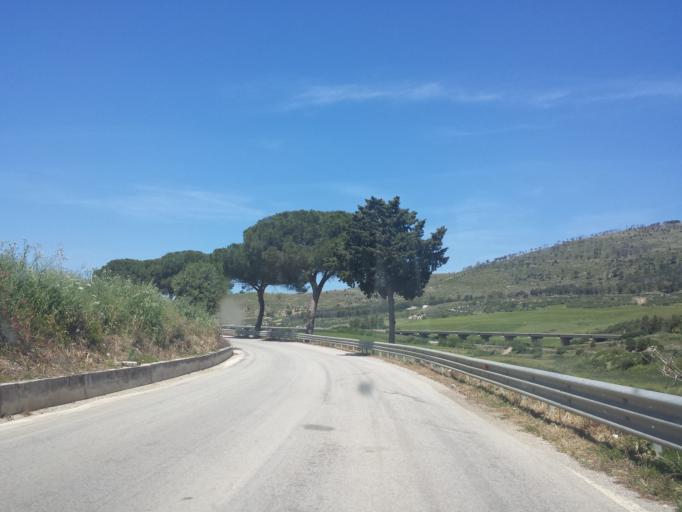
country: IT
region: Sicily
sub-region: Trapani
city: Calatafimi
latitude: 37.9595
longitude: 12.8814
